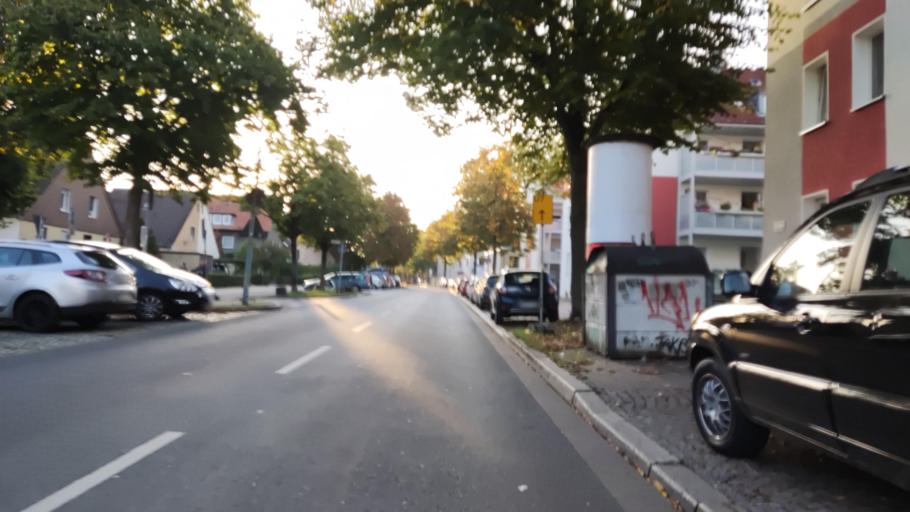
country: DE
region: North Rhine-Westphalia
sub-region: Regierungsbezirk Arnsberg
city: Herne
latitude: 51.5401
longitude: 7.2412
